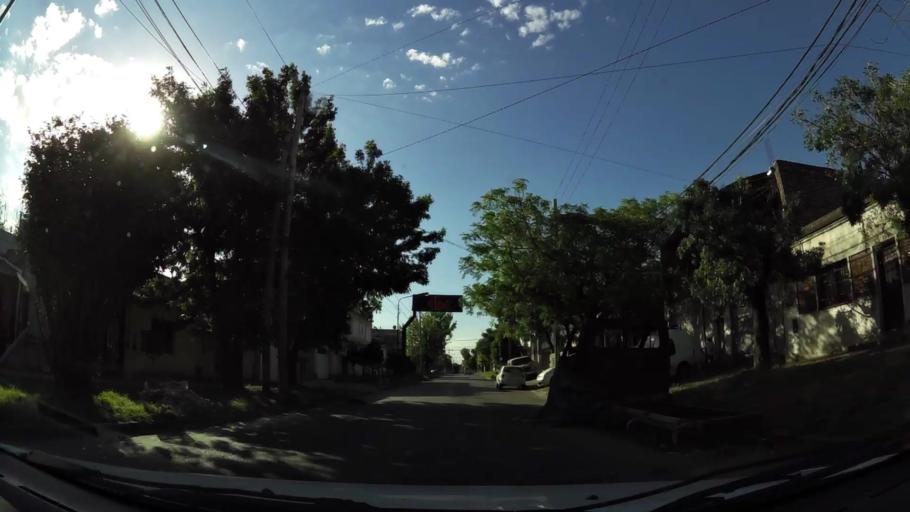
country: AR
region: Buenos Aires
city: Hurlingham
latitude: -34.5696
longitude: -58.6044
